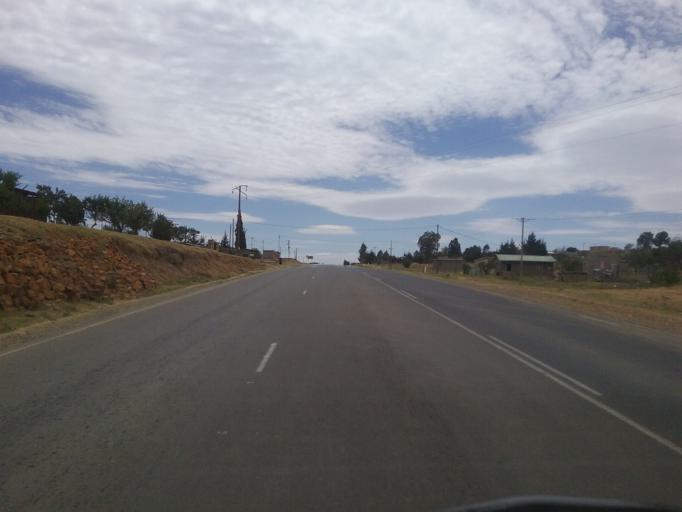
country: LS
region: Maseru
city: Maseru
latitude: -29.4929
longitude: 27.5277
